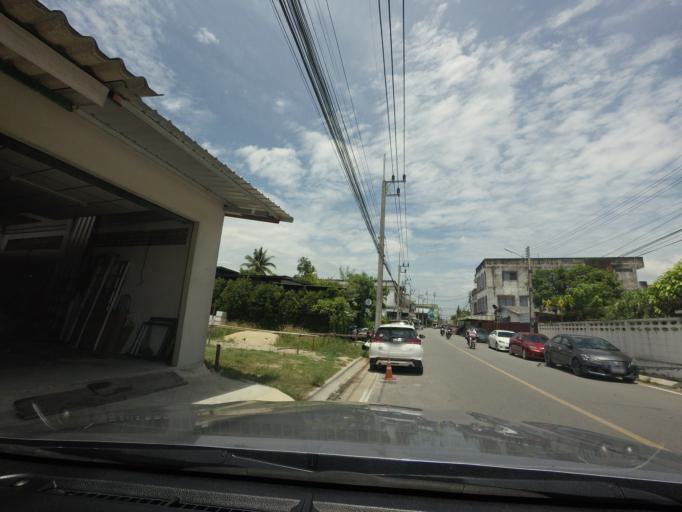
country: TH
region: Yala
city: Yala
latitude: 6.5453
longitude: 101.2942
